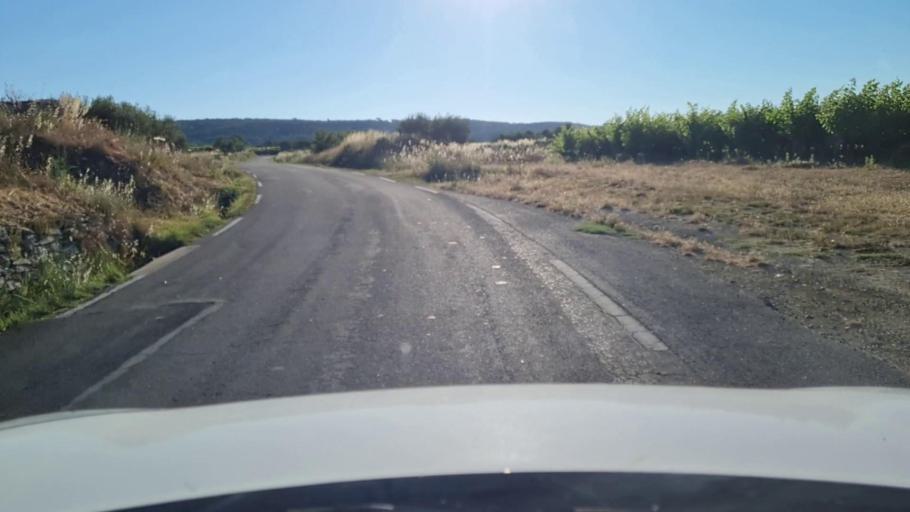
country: FR
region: Languedoc-Roussillon
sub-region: Departement du Gard
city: Clarensac
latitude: 43.8288
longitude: 4.2337
